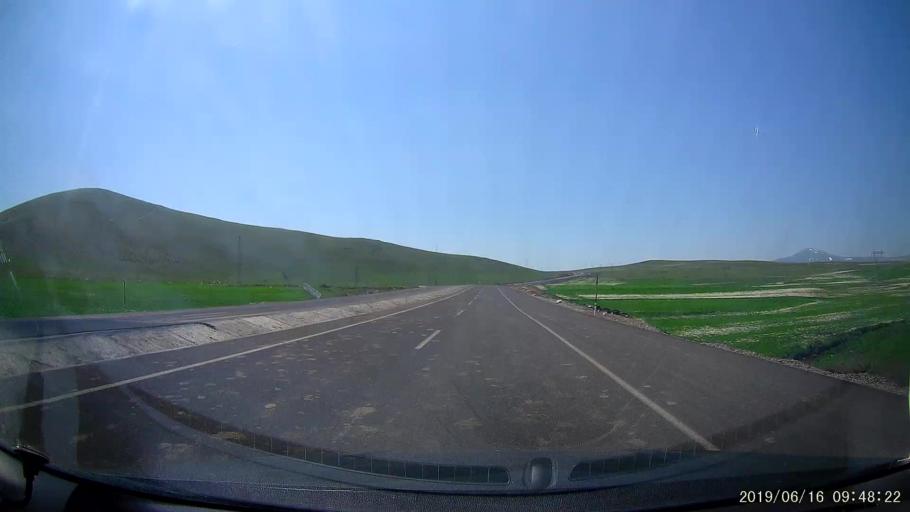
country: TR
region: Kars
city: Digor
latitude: 40.4345
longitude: 43.3522
